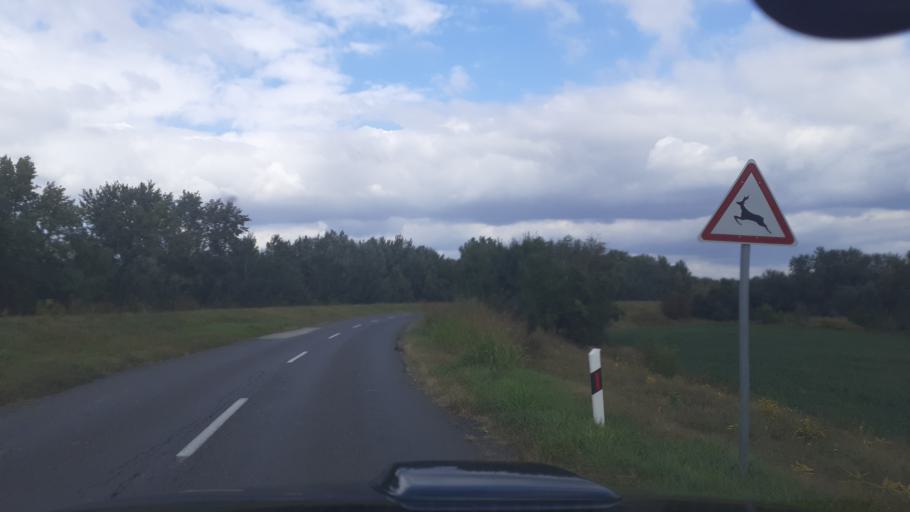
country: HU
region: Bacs-Kiskun
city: Dunavecse
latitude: 46.9265
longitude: 18.9772
